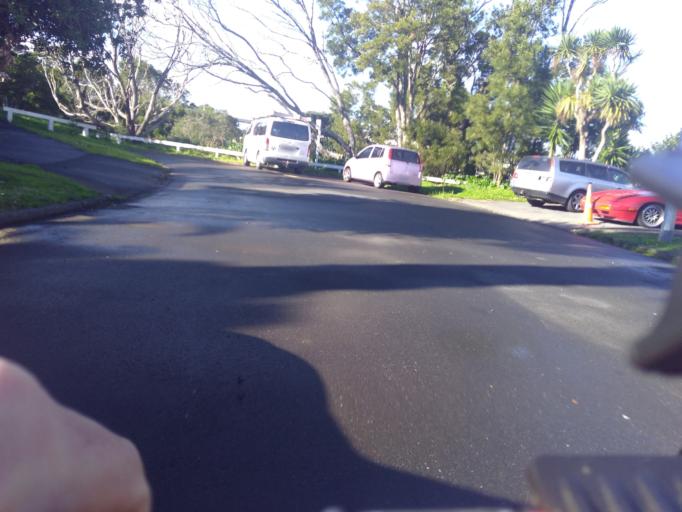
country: NZ
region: Auckland
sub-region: Auckland
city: Rosebank
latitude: -36.8698
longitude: 174.7008
